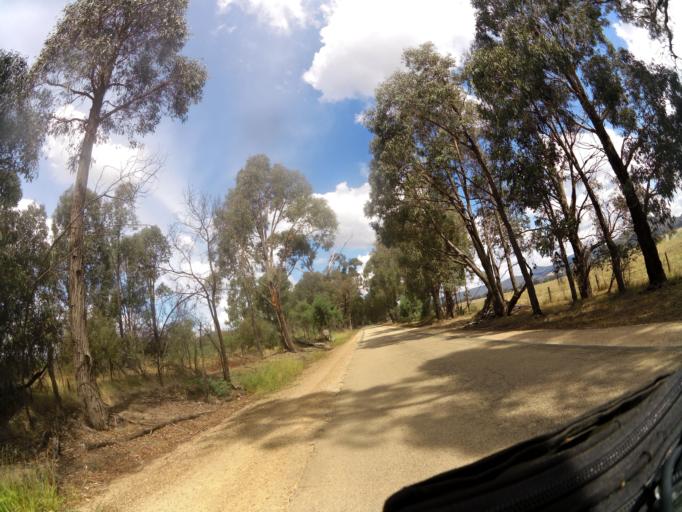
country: AU
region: Victoria
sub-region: Benalla
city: Benalla
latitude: -36.7649
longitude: 145.9763
